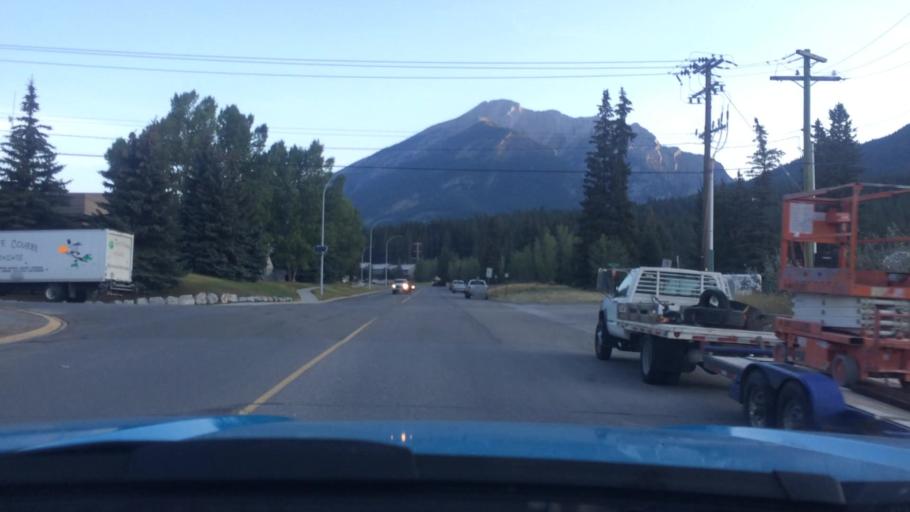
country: CA
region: Alberta
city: Canmore
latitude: 51.0784
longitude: -115.3212
